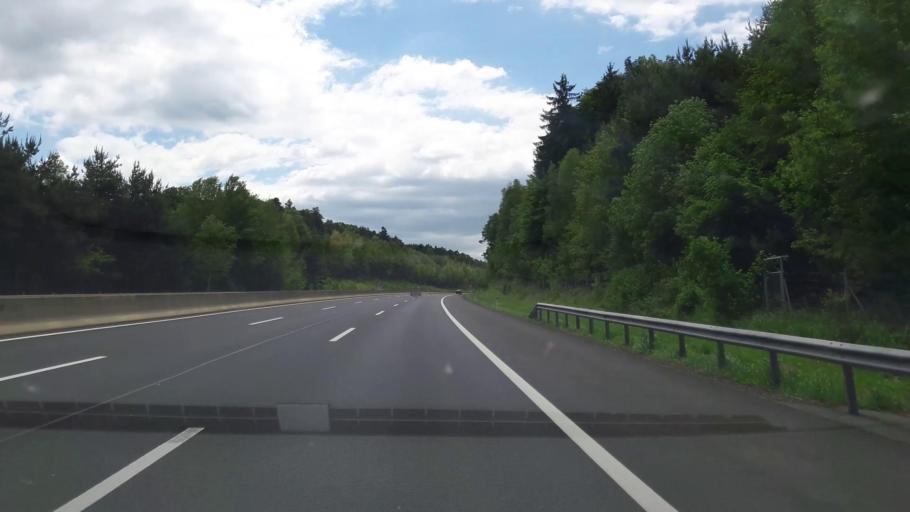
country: AT
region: Styria
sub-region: Politischer Bezirk Hartberg-Fuerstenfeld
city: Bad Waltersdorf
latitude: 47.1599
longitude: 16.0013
